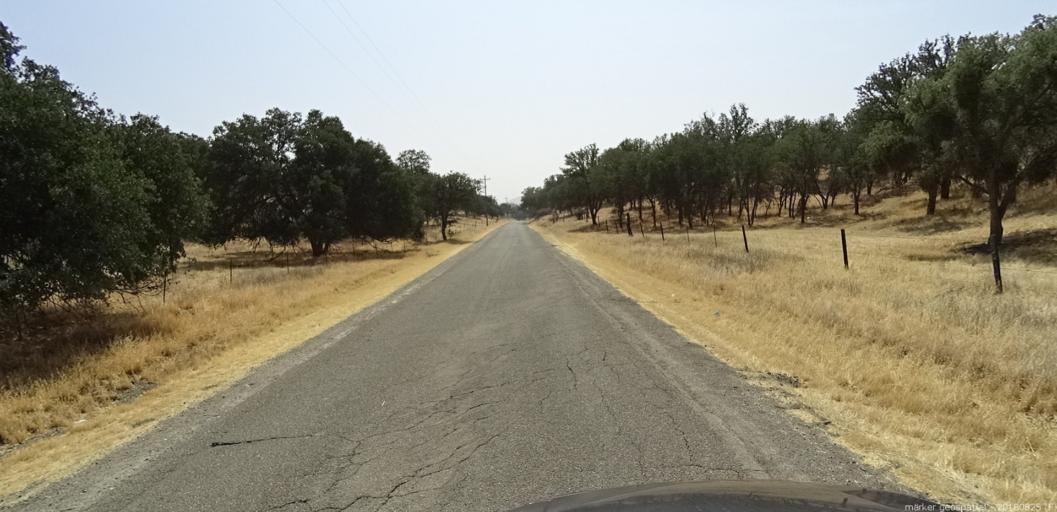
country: US
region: California
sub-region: San Luis Obispo County
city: Shandon
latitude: 35.8626
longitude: -120.3978
